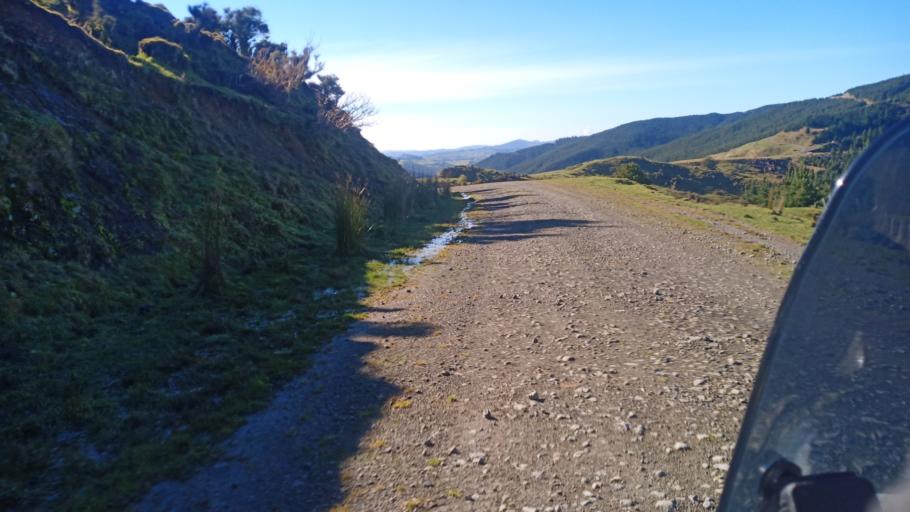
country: NZ
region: Gisborne
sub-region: Gisborne District
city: Gisborne
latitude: -38.1504
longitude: 177.8755
